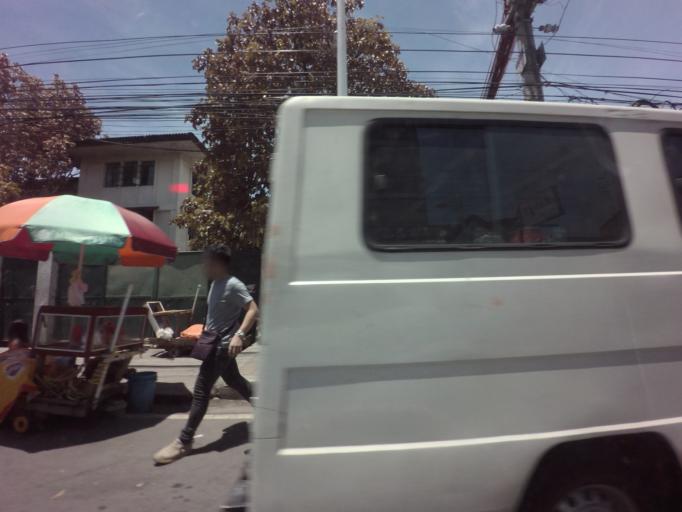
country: PH
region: Metro Manila
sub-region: Makati City
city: Makati City
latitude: 14.5065
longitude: 121.0293
